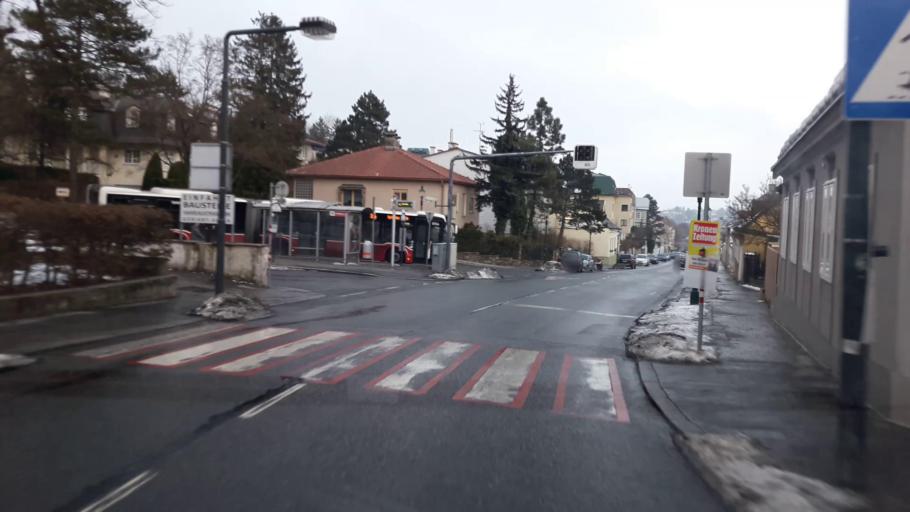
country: AT
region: Lower Austria
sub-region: Politischer Bezirk Wien-Umgebung
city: Klosterneuburg
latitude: 48.2520
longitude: 16.2931
